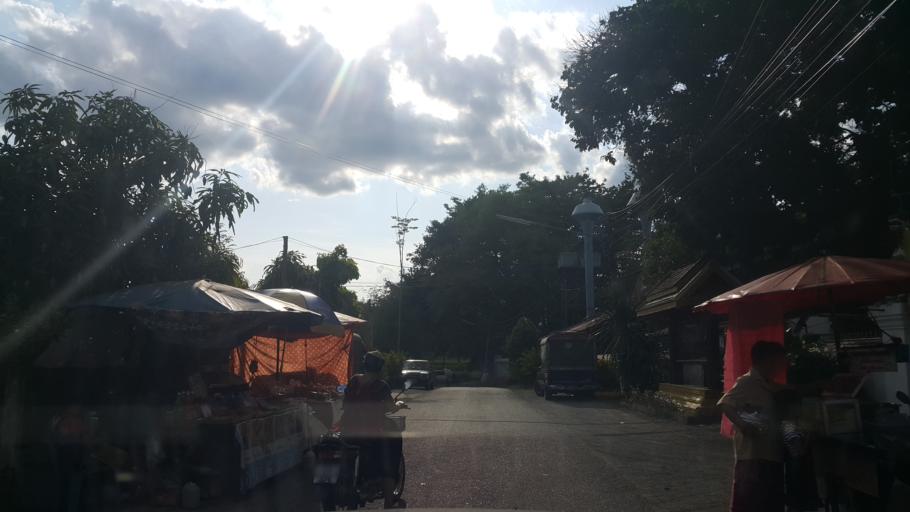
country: TH
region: Chiang Mai
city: Mae On
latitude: 18.7969
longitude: 99.2574
